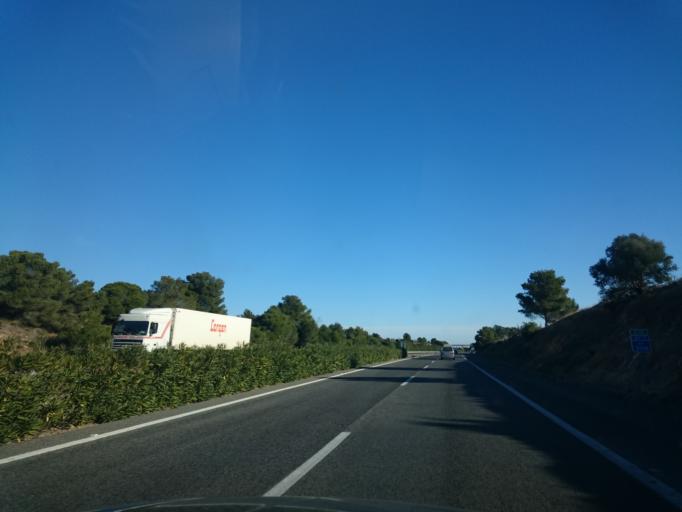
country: ES
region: Catalonia
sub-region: Provincia de Tarragona
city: L'Ampolla
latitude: 40.8262
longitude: 0.7296
